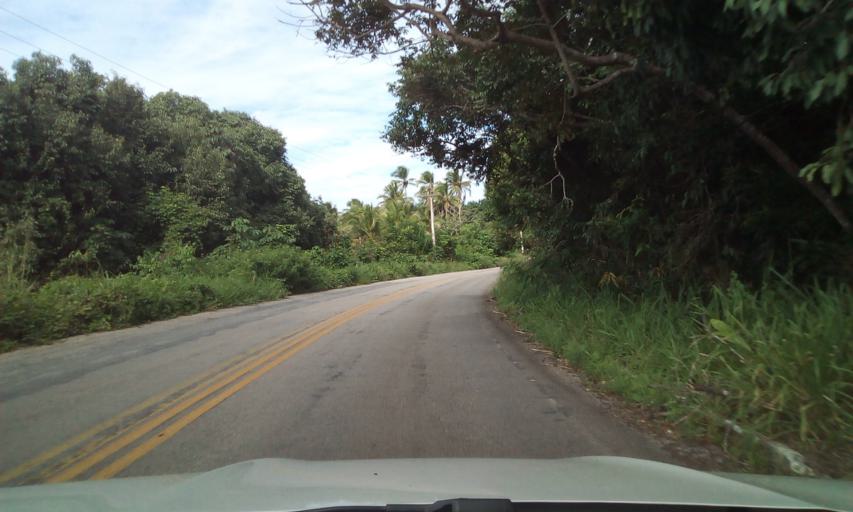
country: BR
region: Paraiba
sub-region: Cabedelo
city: Cabedelo
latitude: -6.9442
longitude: -34.9166
